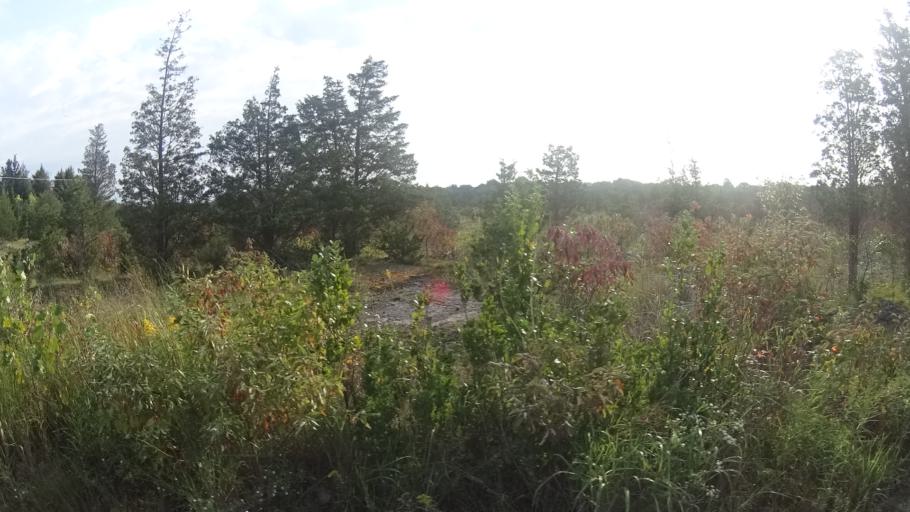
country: US
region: Ohio
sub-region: Erie County
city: Sandusky
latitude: 41.6009
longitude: -82.7178
